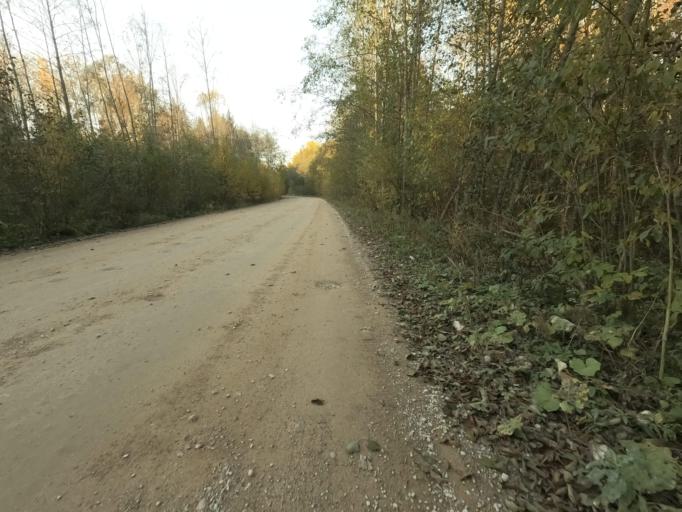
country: RU
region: Leningrad
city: Lyuban'
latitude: 58.9954
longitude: 31.1058
